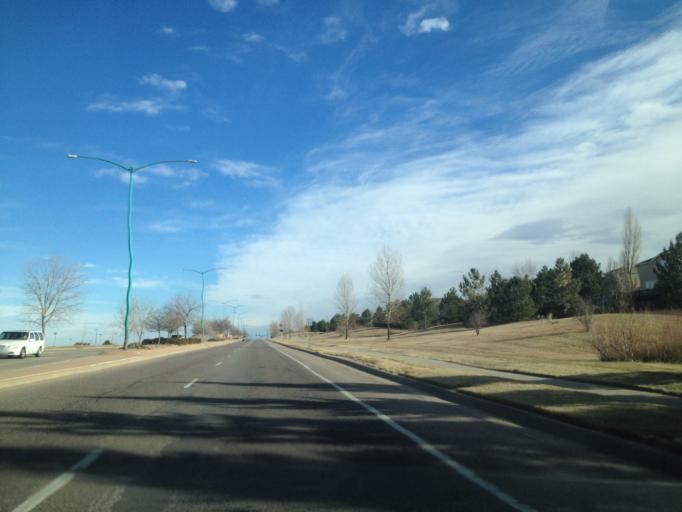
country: US
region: Colorado
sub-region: Boulder County
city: Superior
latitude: 39.9292
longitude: -105.1594
